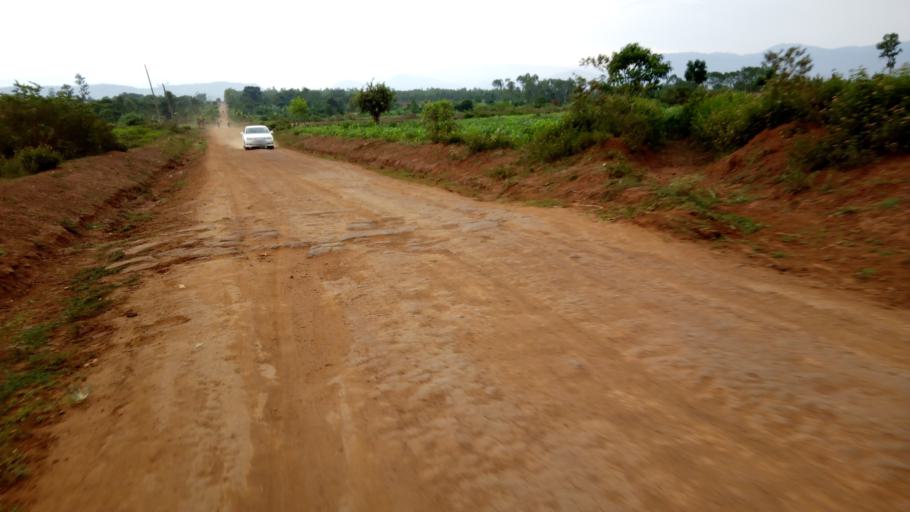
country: UG
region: Eastern Region
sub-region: Mbale District
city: Mbale
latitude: 1.1413
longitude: 34.1337
